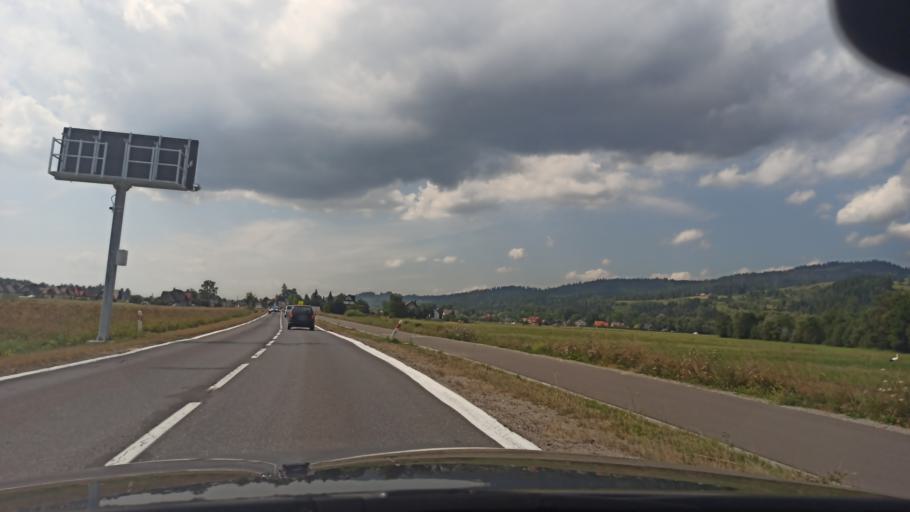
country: PL
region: Lesser Poland Voivodeship
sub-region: Powiat nowotarski
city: Frydman
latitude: 49.4727
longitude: 20.1829
